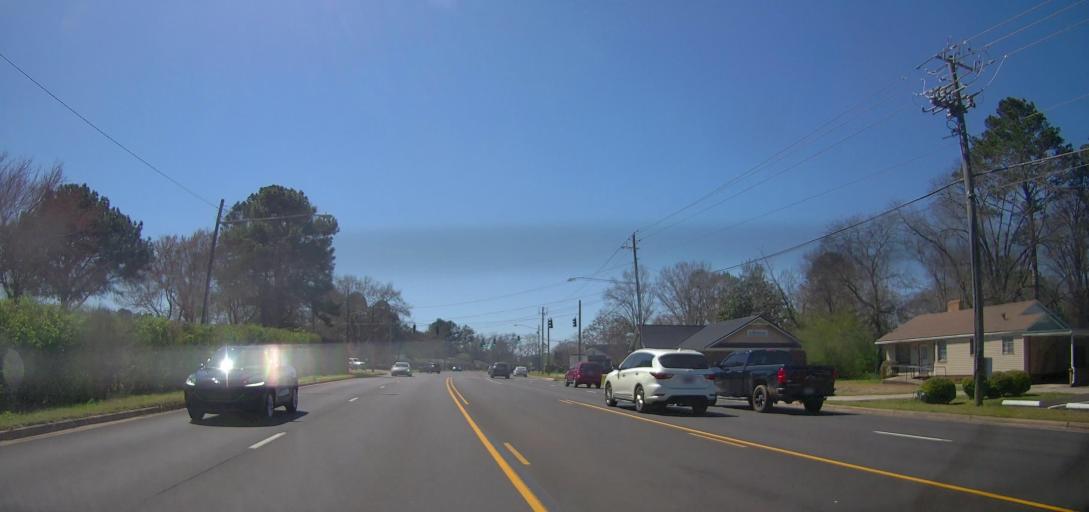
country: US
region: Alabama
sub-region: Etowah County
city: Rainbow City
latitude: 33.9697
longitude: -86.0212
